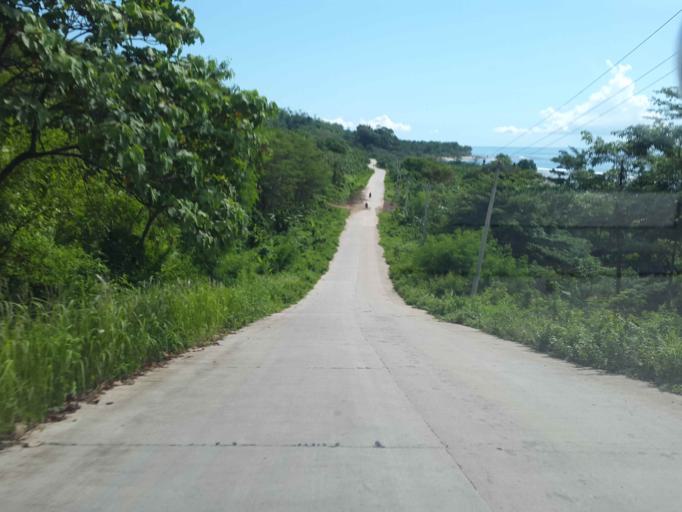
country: ID
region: Banten
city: Babakanbungur
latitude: -6.5203
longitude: 105.6306
